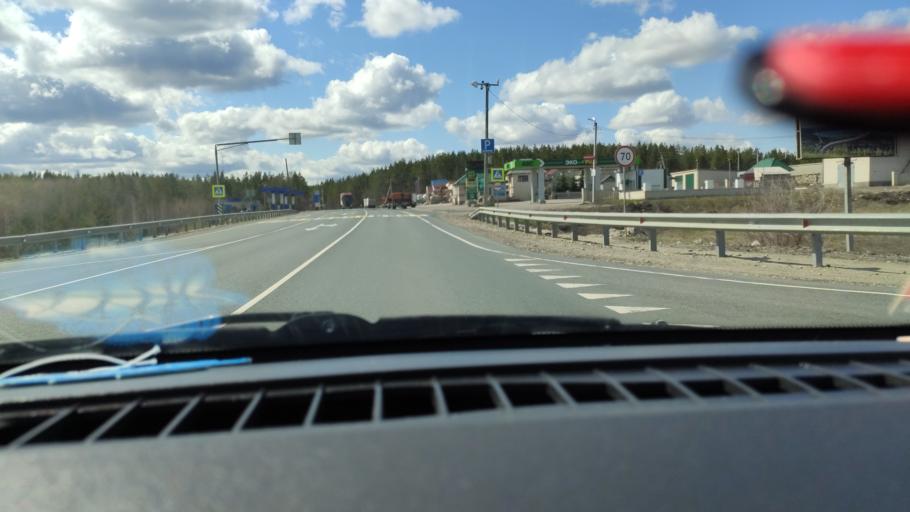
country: RU
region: Saratov
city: Khvalynsk
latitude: 52.5233
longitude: 48.0210
